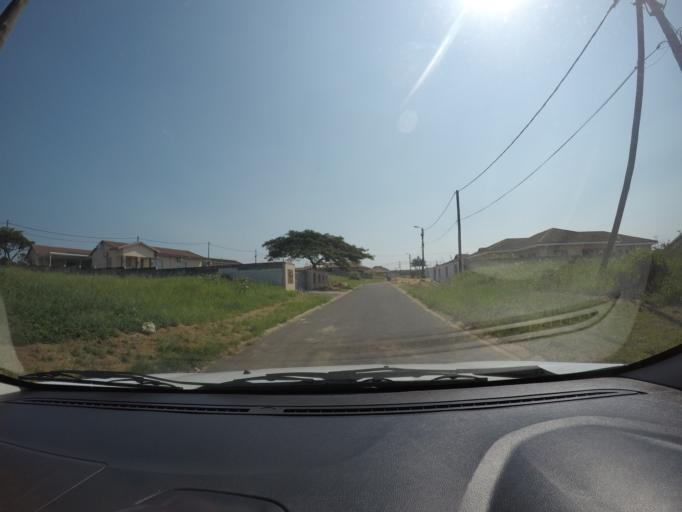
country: ZA
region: KwaZulu-Natal
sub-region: uThungulu District Municipality
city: Richards Bay
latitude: -28.7249
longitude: 32.0379
